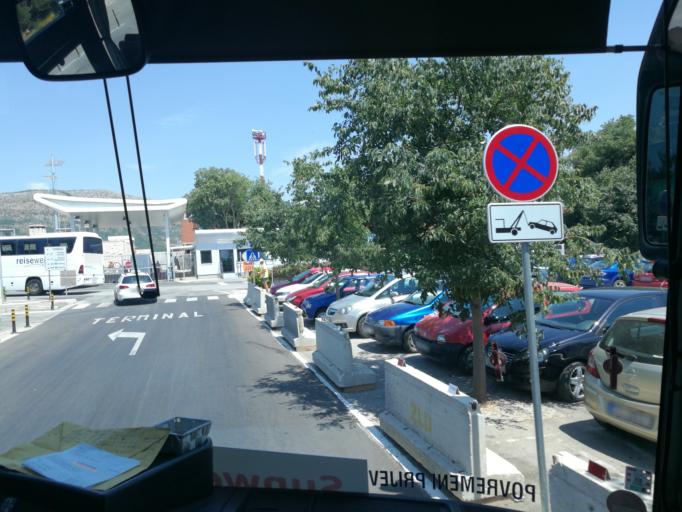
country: HR
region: Dubrovacko-Neretvanska
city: Jasenice
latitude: 42.5590
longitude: 18.2636
